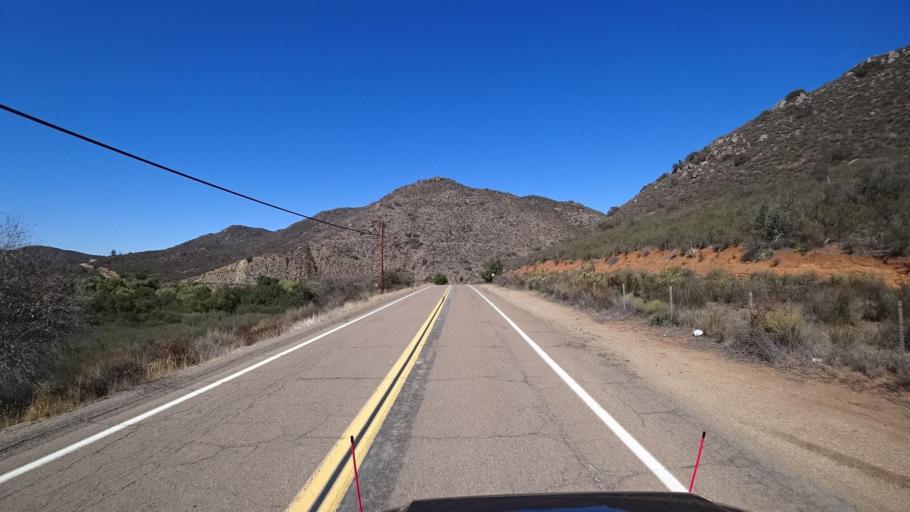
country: US
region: California
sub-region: San Diego County
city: Alpine
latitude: 32.7977
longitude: -116.7473
